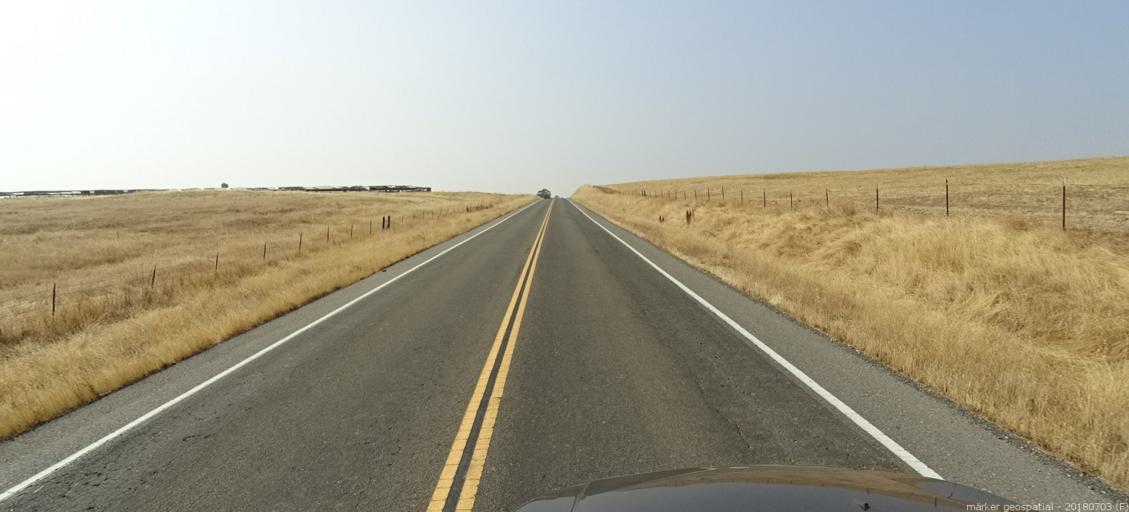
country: US
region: California
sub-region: Madera County
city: Bonadelle Ranchos-Madera Ranchos
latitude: 37.0043
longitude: -119.7360
